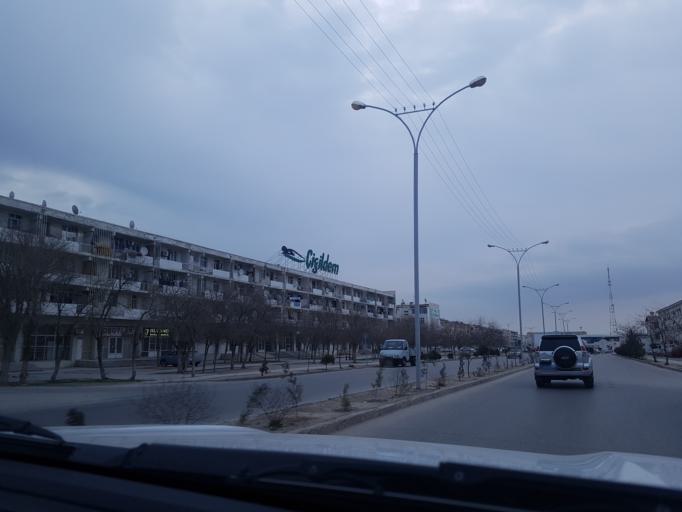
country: TM
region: Balkan
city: Balkanabat
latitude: 39.5227
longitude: 54.3539
